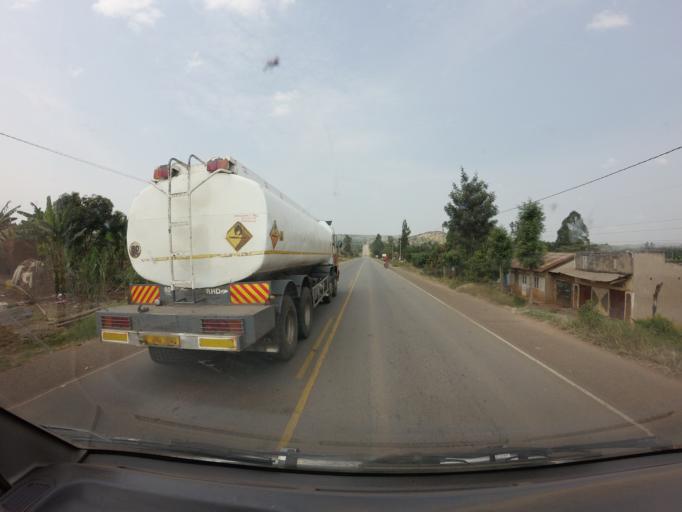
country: UG
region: Central Region
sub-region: Lwengo District
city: Lwengo
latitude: -0.3933
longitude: 31.3372
